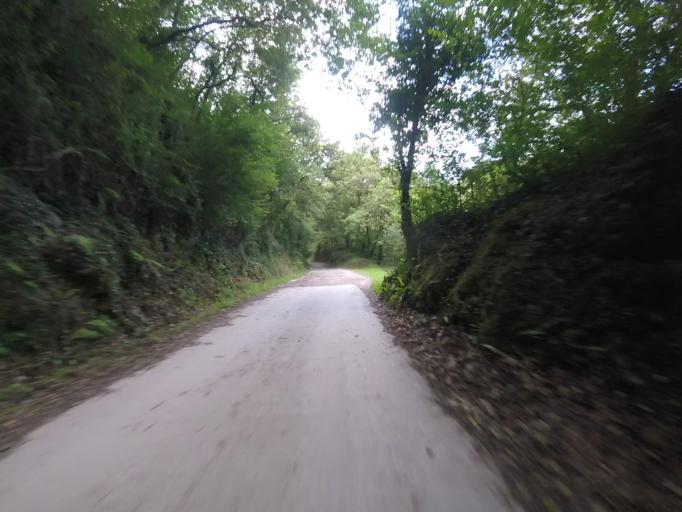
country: ES
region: Basque Country
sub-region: Provincia de Guipuzcoa
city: Andoain
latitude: 43.1901
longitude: -2.0054
